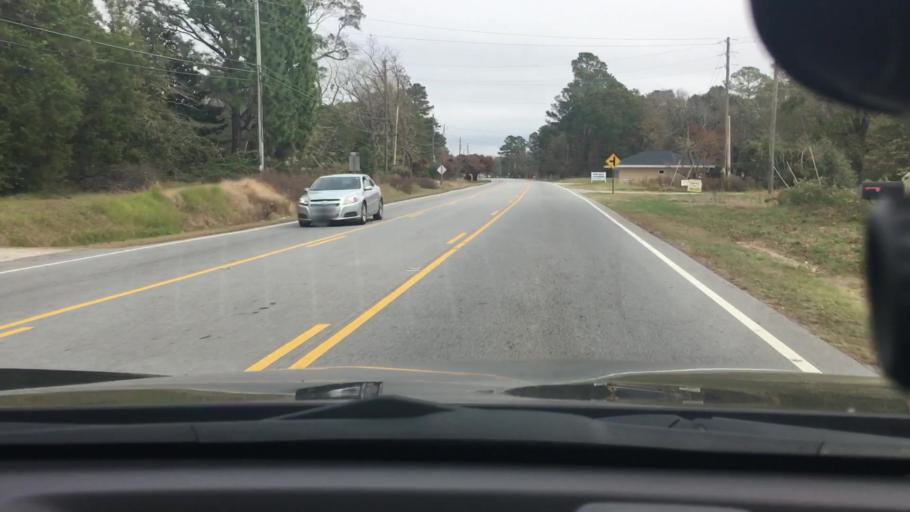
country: US
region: North Carolina
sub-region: Pitt County
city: Greenville
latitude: 35.6272
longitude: -77.3419
